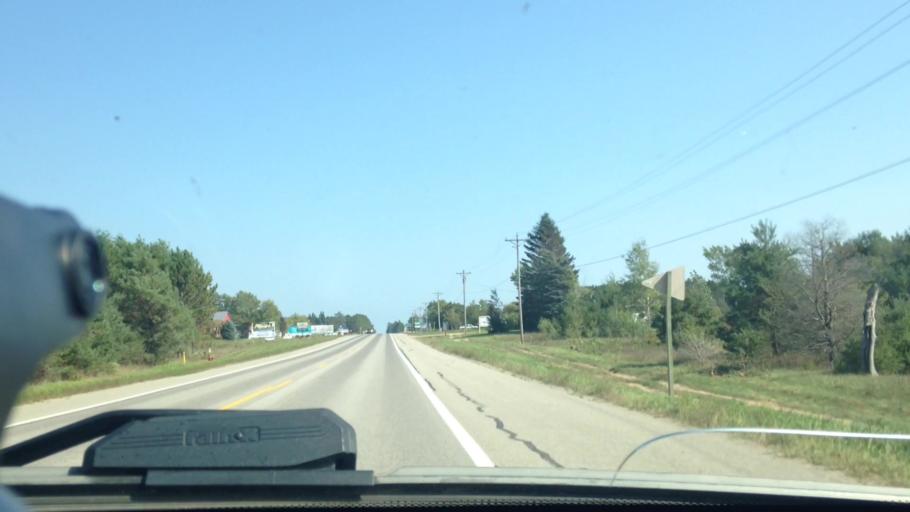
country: US
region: Michigan
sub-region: Luce County
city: Newberry
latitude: 46.3037
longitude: -85.4964
